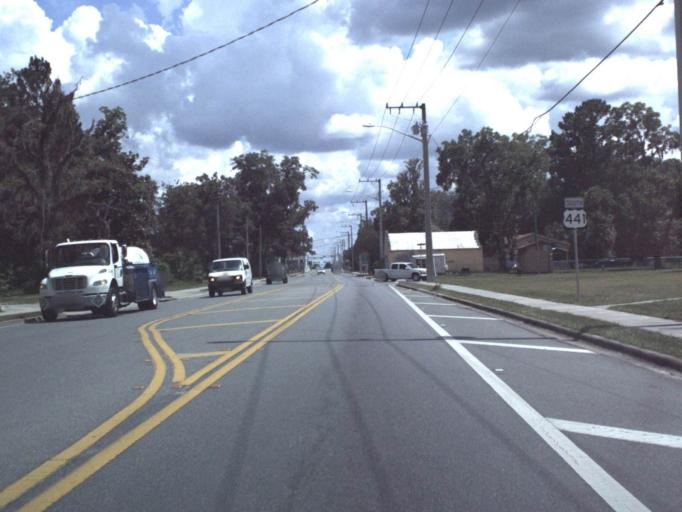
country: US
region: Florida
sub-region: Columbia County
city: Five Points
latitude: 30.2030
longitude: -82.6374
